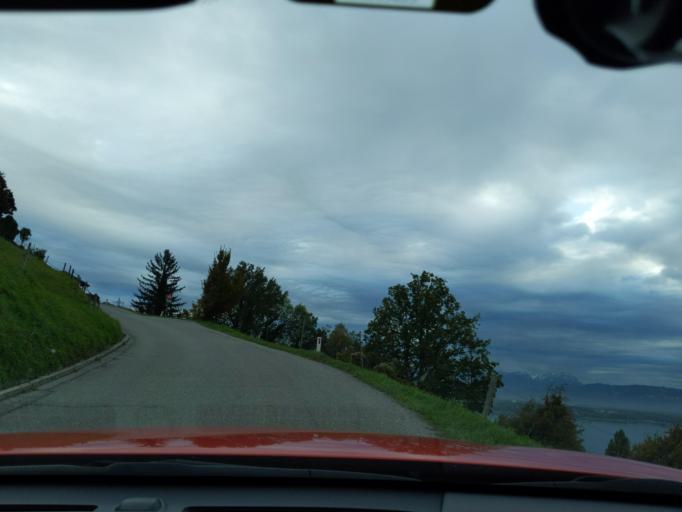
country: AT
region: Vorarlberg
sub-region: Politischer Bezirk Bregenz
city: Lochau
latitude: 47.5271
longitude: 9.7570
